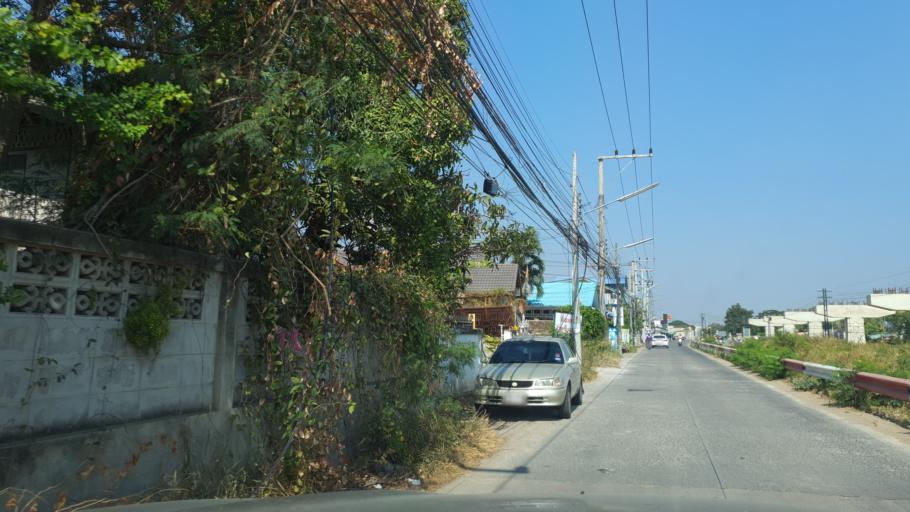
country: TH
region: Prachuap Khiri Khan
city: Hua Hin
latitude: 12.5591
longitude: 99.9564
